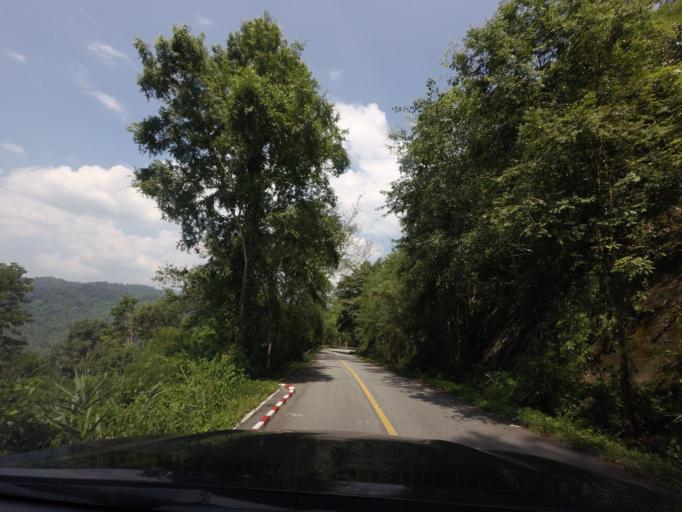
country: TH
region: Loei
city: Na Haeo
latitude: 17.6311
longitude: 100.9028
